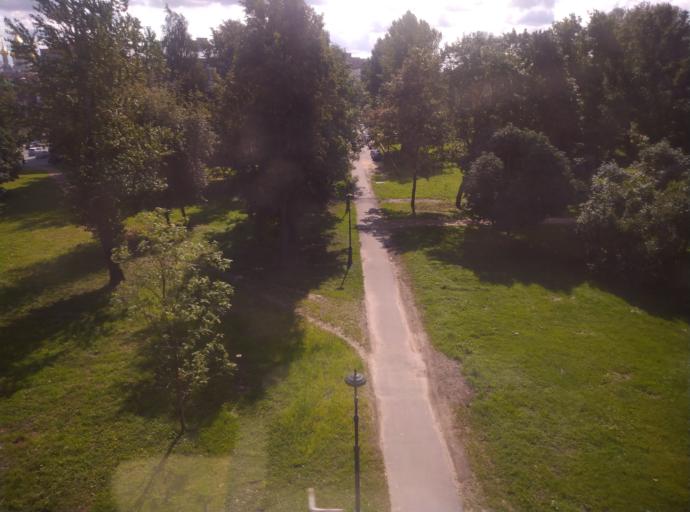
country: RU
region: St.-Petersburg
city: Centralniy
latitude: 59.9136
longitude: 30.4037
